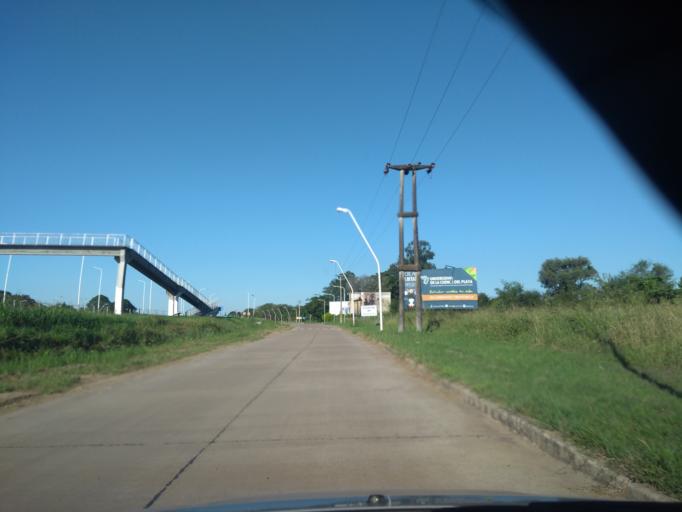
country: AR
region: Chaco
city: Barranqueras
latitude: -27.4366
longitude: -58.9185
